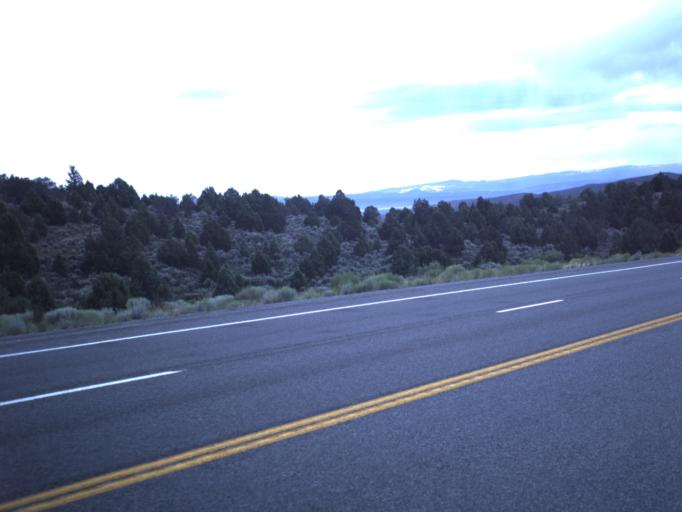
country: US
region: Utah
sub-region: Garfield County
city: Panguitch
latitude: 38.0286
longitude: -112.5311
